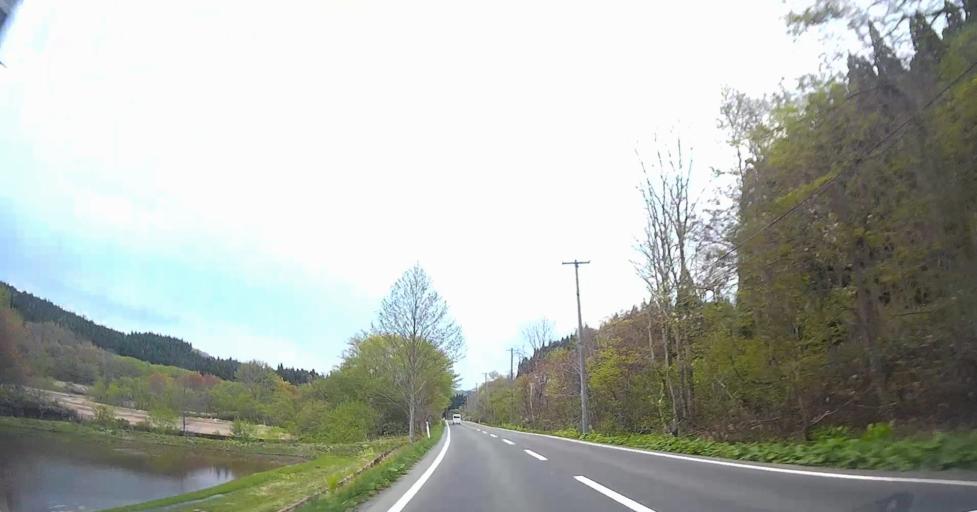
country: JP
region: Aomori
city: Goshogawara
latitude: 41.1239
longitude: 140.5203
